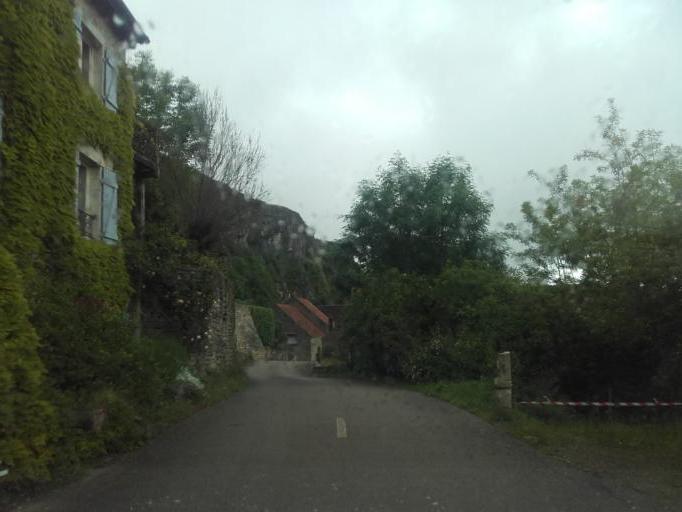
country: FR
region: Bourgogne
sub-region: Departement de la Cote-d'Or
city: Nolay
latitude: 46.9890
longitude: 4.6877
